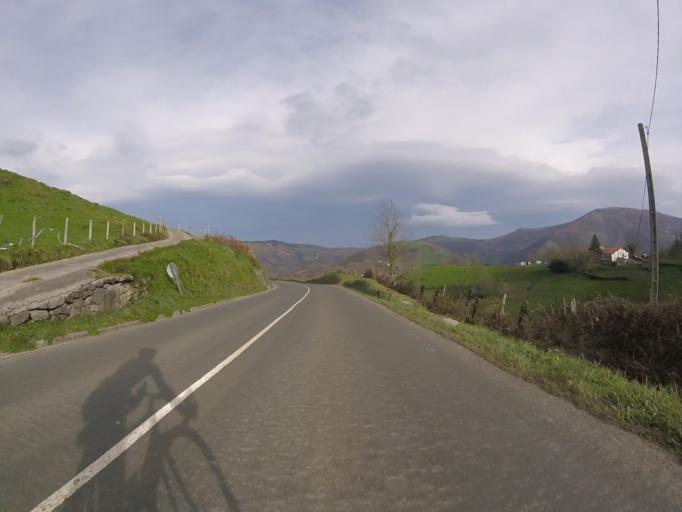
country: ES
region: Basque Country
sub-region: Provincia de Guipuzcoa
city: Beizama
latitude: 43.1661
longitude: -2.2218
